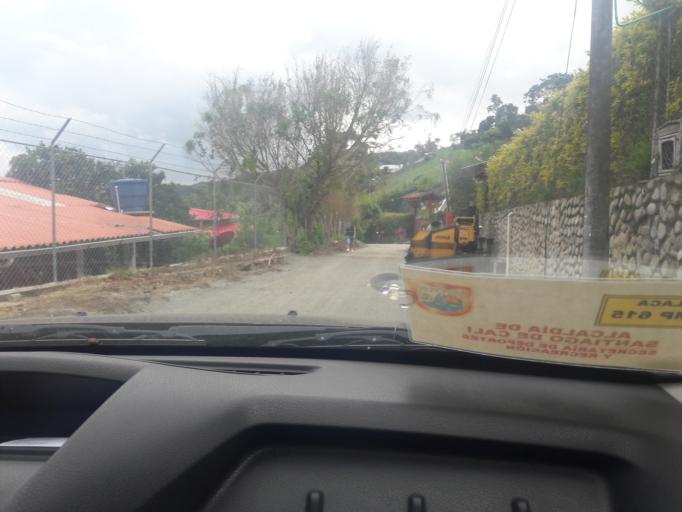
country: CO
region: Valle del Cauca
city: Cali
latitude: 3.4677
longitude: -76.6329
